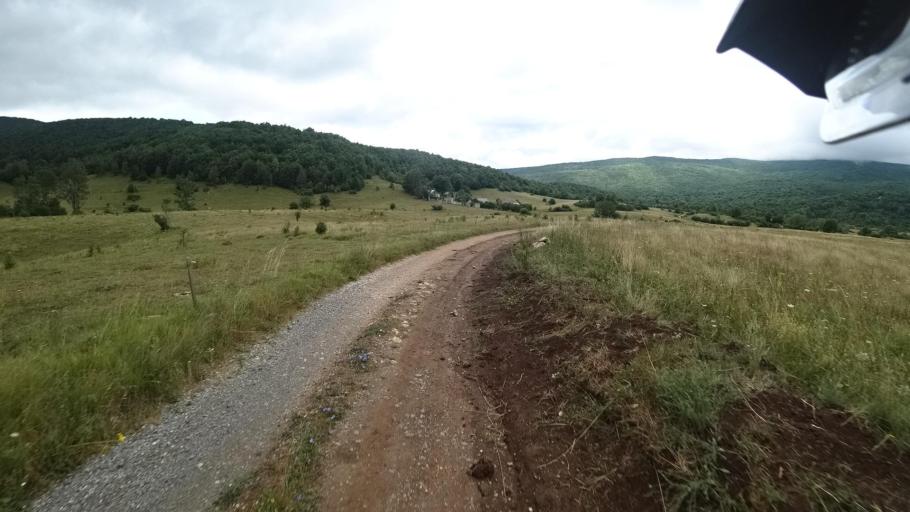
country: HR
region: Licko-Senjska
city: Jezerce
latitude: 44.7772
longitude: 15.4935
